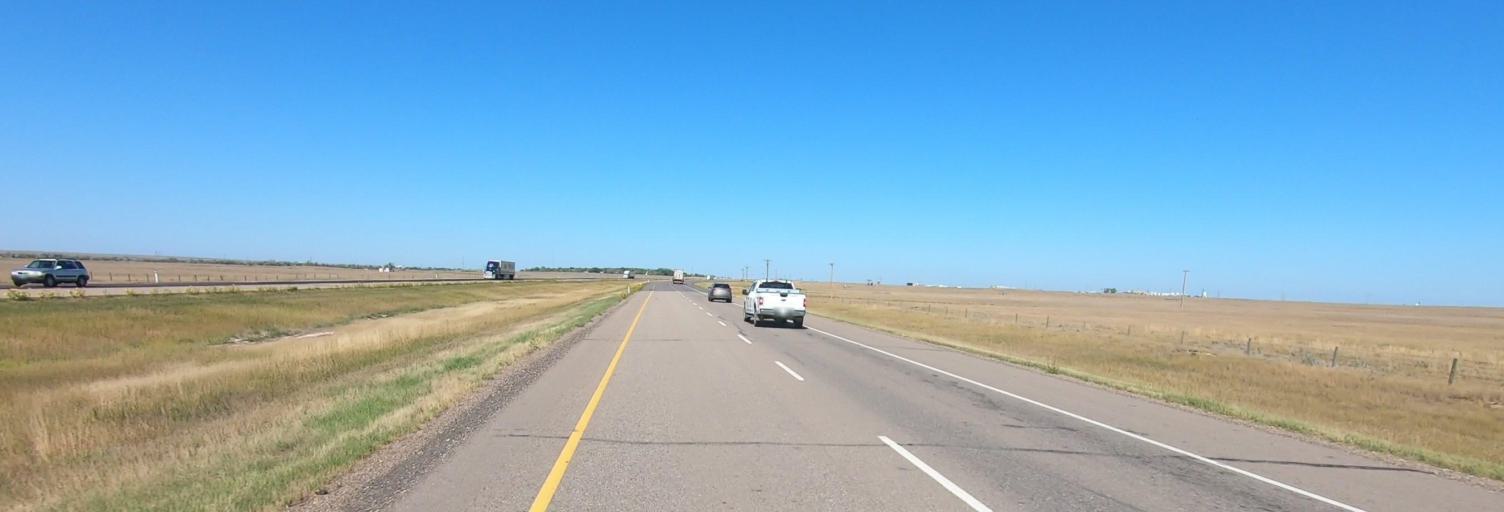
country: CA
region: Alberta
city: Brooks
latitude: 50.5287
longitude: -111.7791
